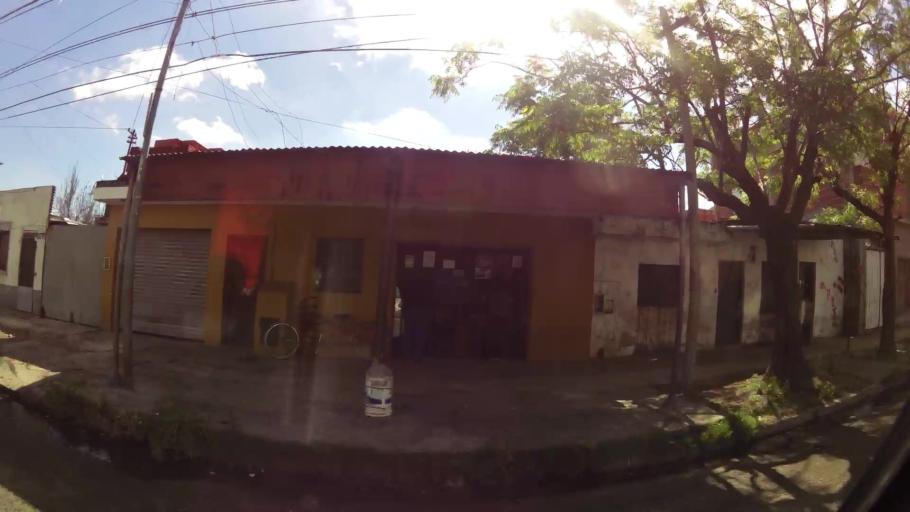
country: AR
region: Buenos Aires F.D.
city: Villa Lugano
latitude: -34.6777
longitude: -58.4311
